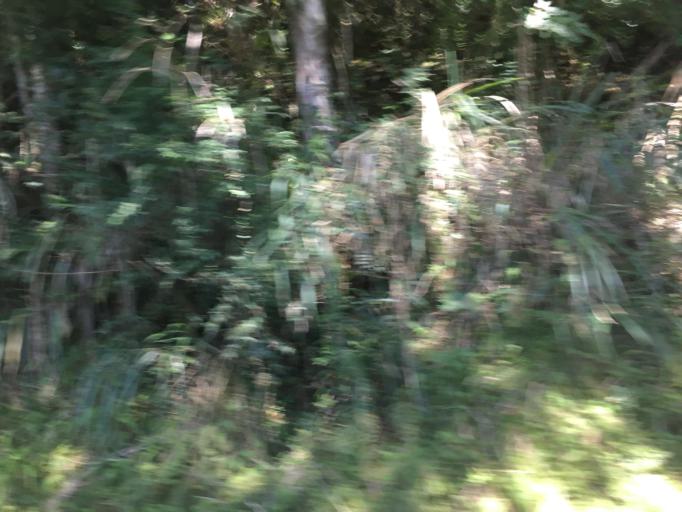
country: TW
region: Taiwan
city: Daxi
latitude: 24.6052
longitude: 121.4572
